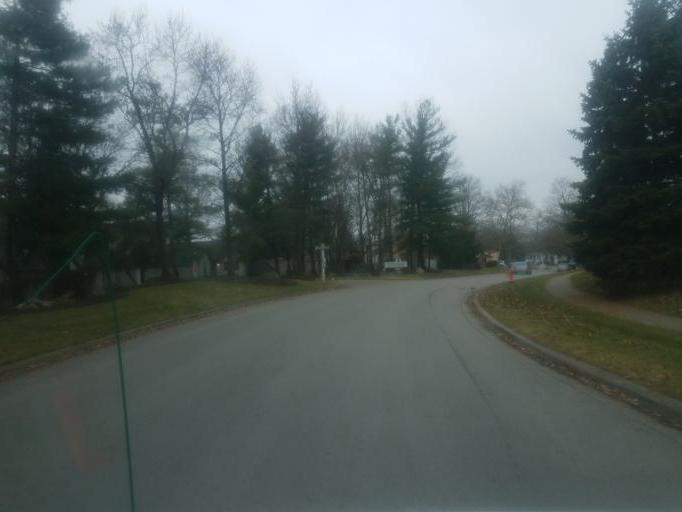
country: US
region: Ohio
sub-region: Franklin County
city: Minerva Park
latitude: 40.0981
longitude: -82.9451
